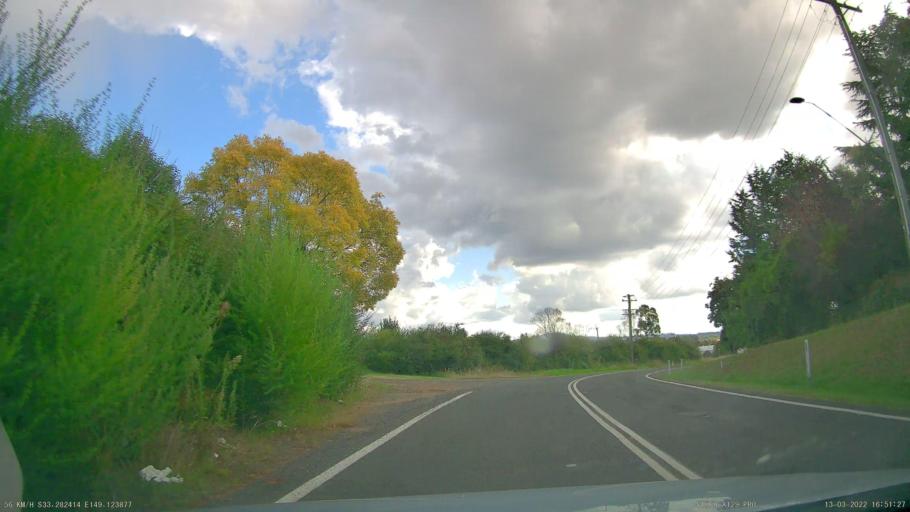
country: AU
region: New South Wales
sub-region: Orange Municipality
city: Orange
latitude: -33.2825
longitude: 149.1237
